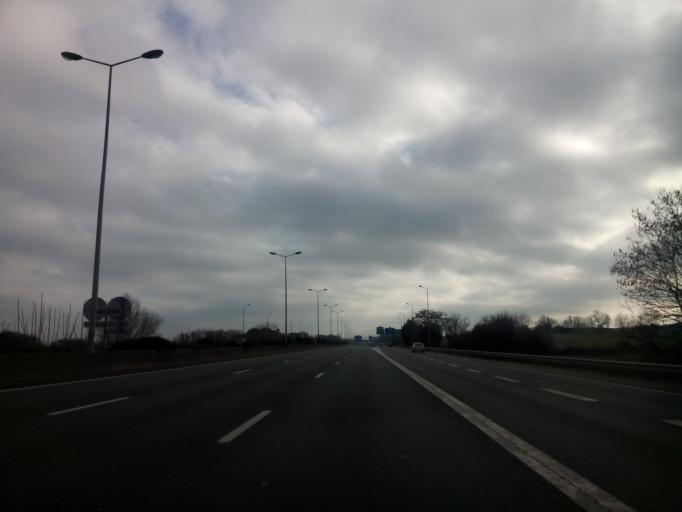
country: FR
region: Rhone-Alpes
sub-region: Departement du Rhone
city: Saint-Priest
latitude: 45.7057
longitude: 4.9596
